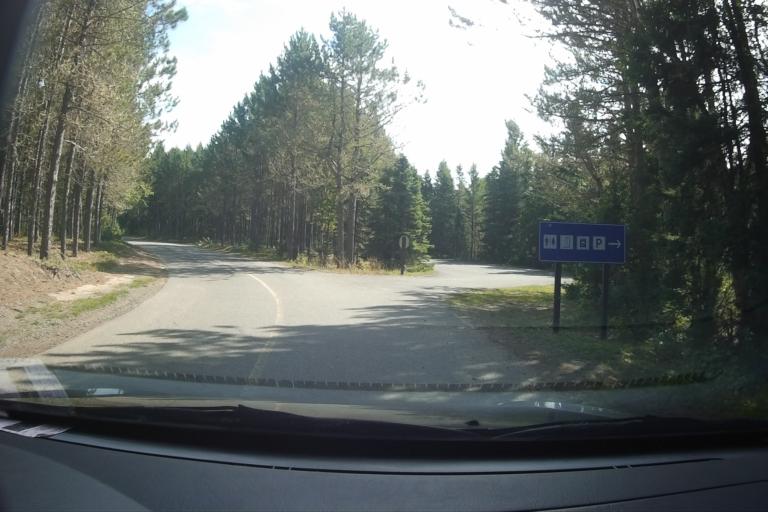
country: CA
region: Ontario
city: Marathon
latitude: 48.7863
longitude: -86.6209
